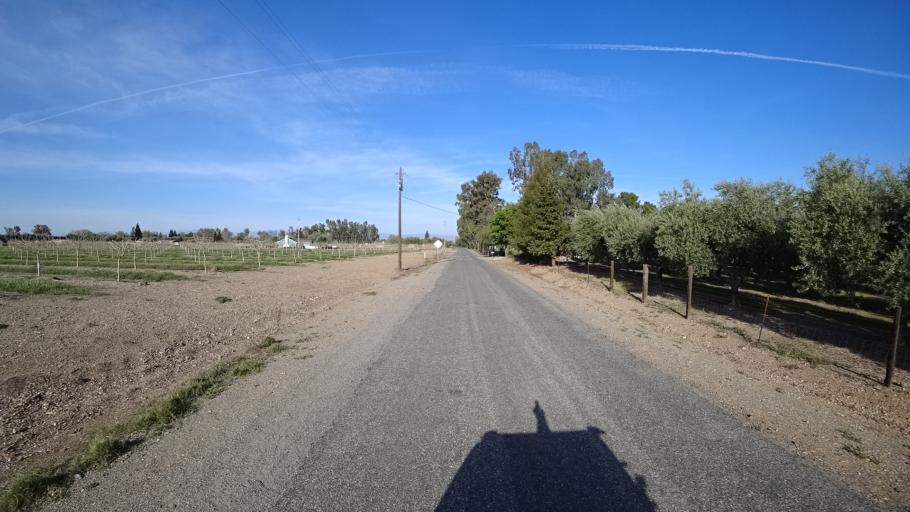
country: US
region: California
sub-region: Glenn County
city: Orland
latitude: 39.7151
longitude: -122.2125
